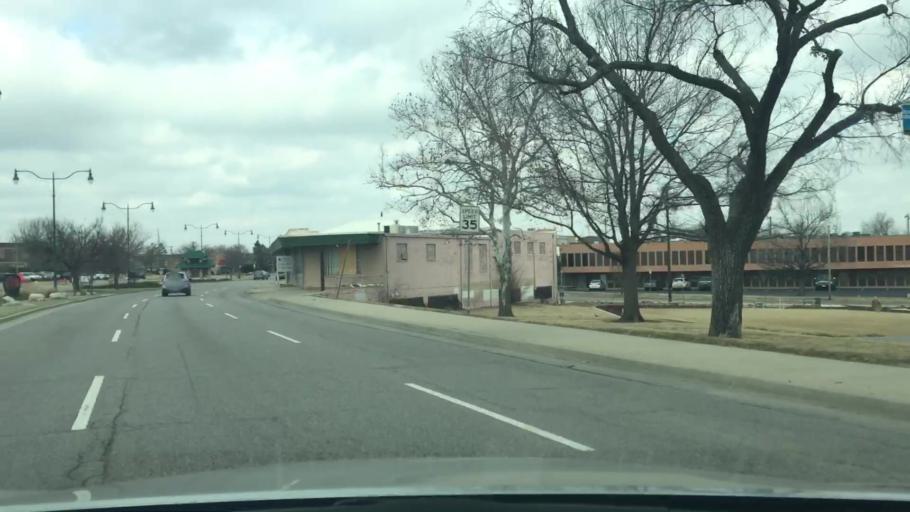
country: US
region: Oklahoma
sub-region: Oklahoma County
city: Oklahoma City
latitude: 35.4945
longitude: -97.5326
